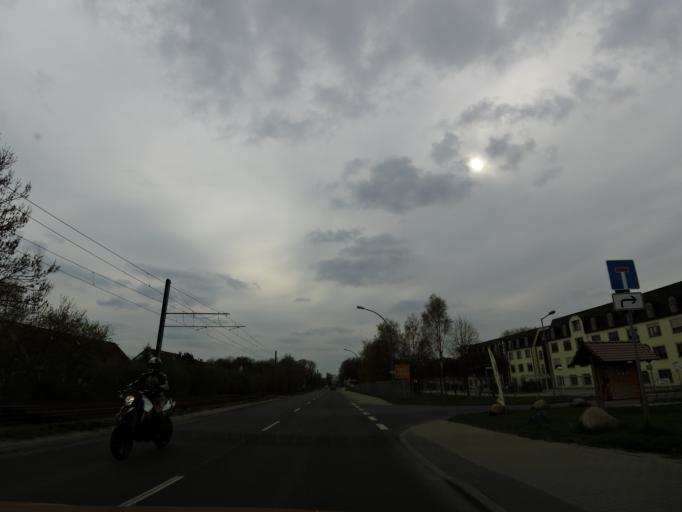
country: DE
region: Brandenburg
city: Mullrose
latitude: 52.2970
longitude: 14.4721
